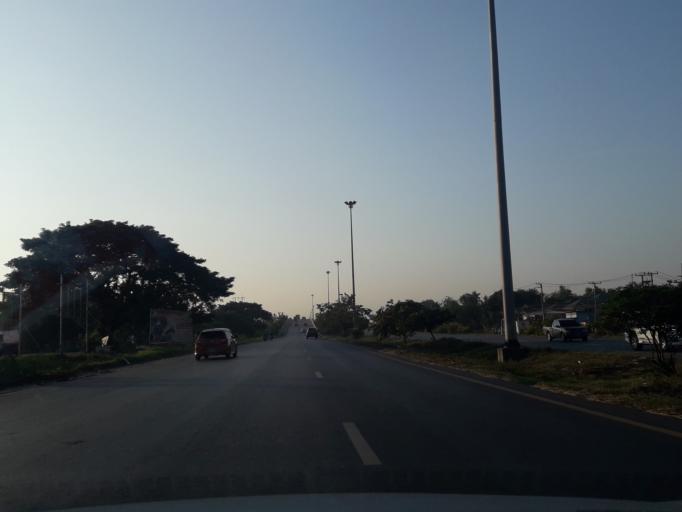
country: TH
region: Phra Nakhon Si Ayutthaya
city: Bang Pa-in
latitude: 14.1981
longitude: 100.5510
